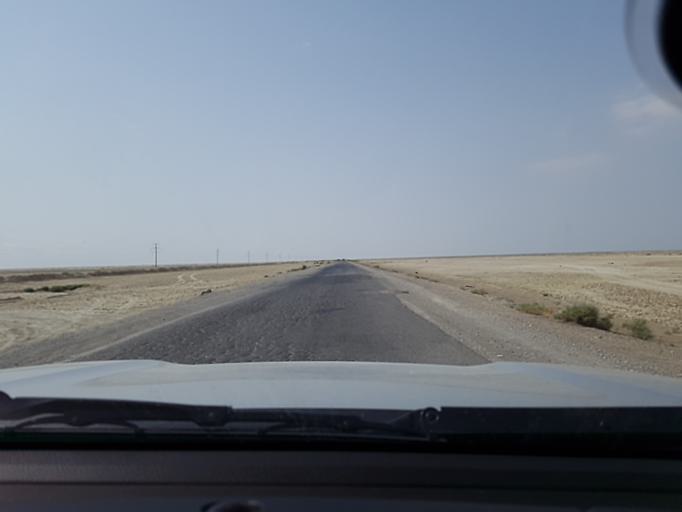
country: TM
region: Balkan
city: Gumdag
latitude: 38.9933
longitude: 54.5866
